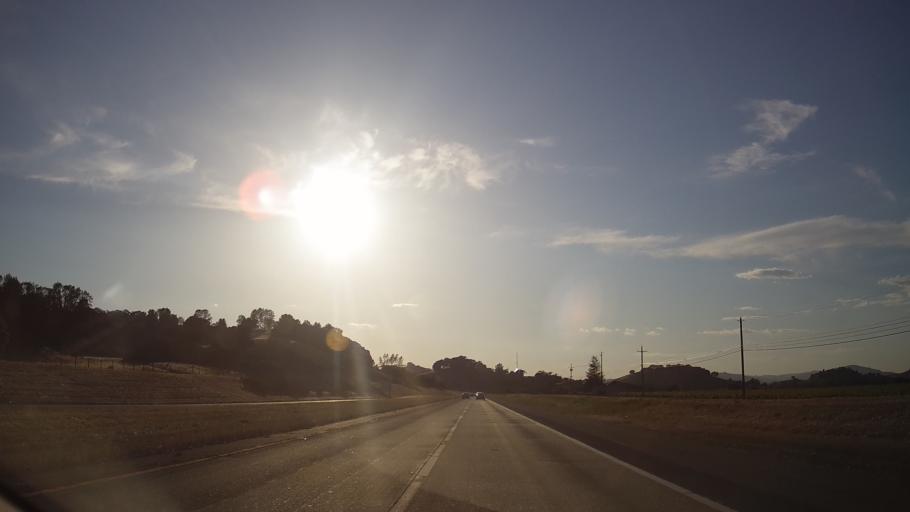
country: US
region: California
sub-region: Sonoma County
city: Cloverdale
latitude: 38.7245
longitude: -122.9321
